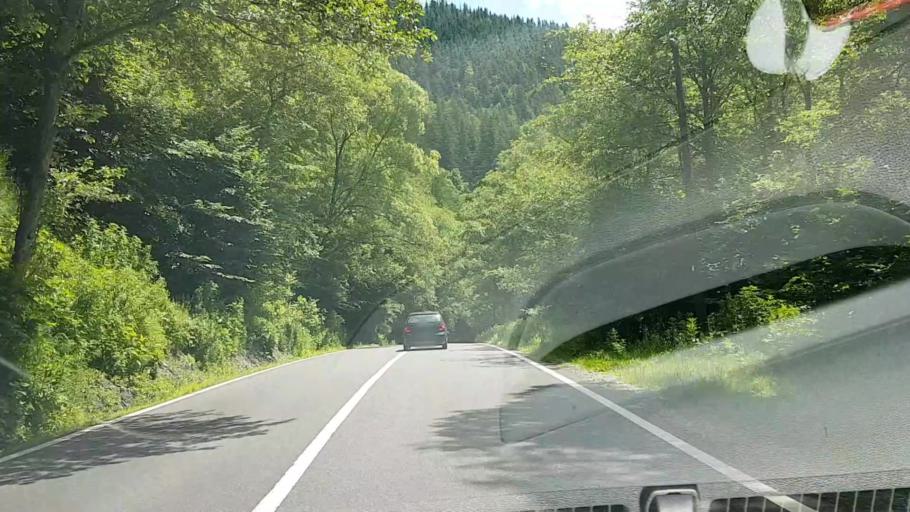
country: RO
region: Suceava
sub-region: Comuna Brosteni
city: Brosteni
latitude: 47.2823
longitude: 25.6482
